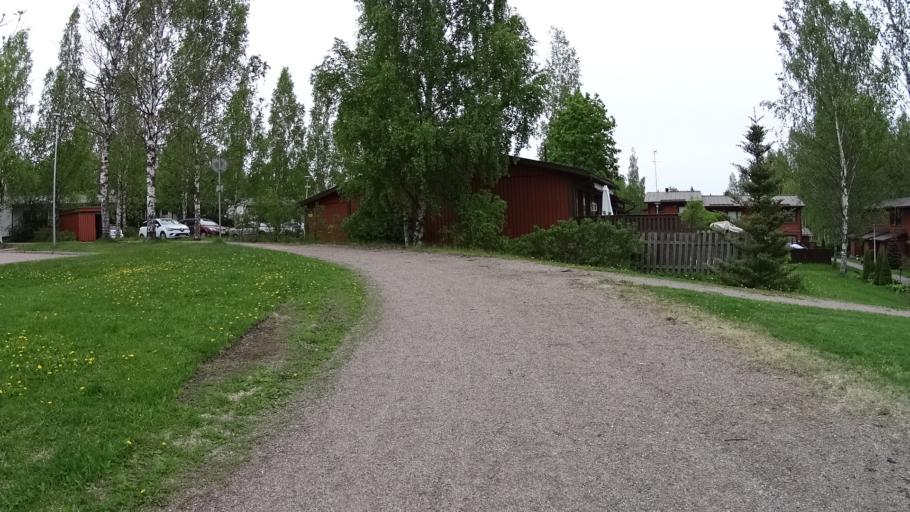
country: FI
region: Uusimaa
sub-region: Helsinki
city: Kilo
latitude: 60.2666
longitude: 24.7938
